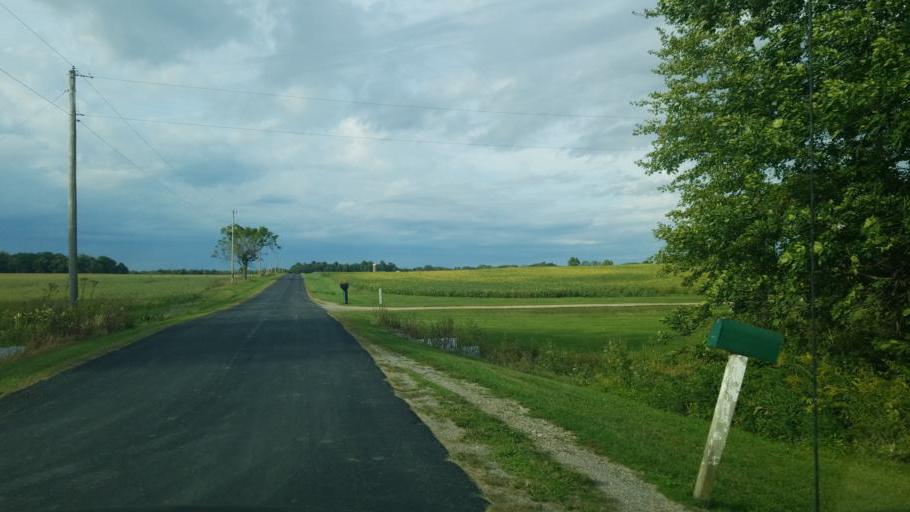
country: US
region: Ohio
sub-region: Wyandot County
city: Upper Sandusky
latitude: 40.9296
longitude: -83.1503
